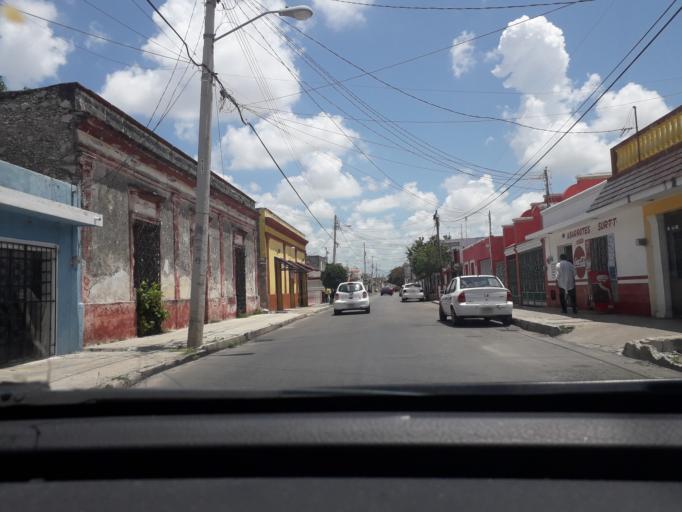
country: MX
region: Yucatan
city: Merida
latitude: 20.9549
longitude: -89.6206
